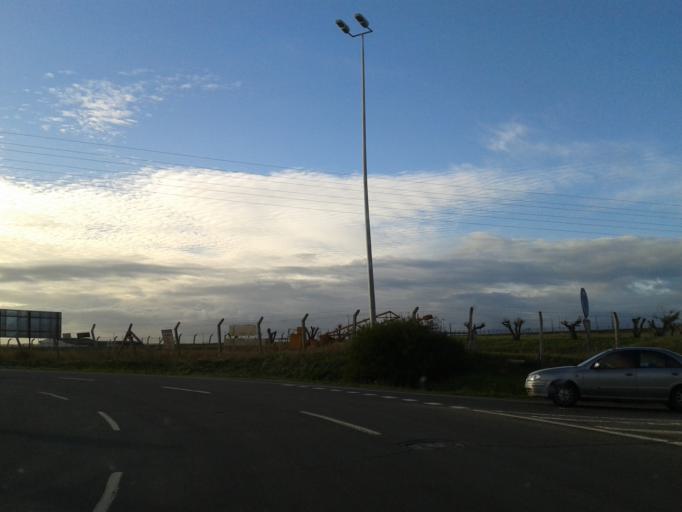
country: PT
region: Beja
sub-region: Beja
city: Beja
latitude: 38.0260
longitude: -7.8749
